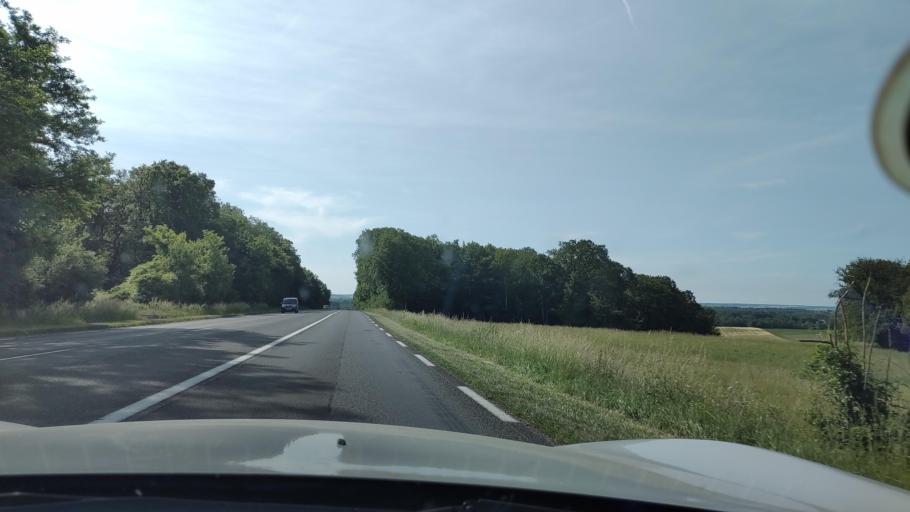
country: FR
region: Ile-de-France
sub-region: Departement de Seine-et-Marne
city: Sourdun
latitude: 48.5207
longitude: 3.4157
